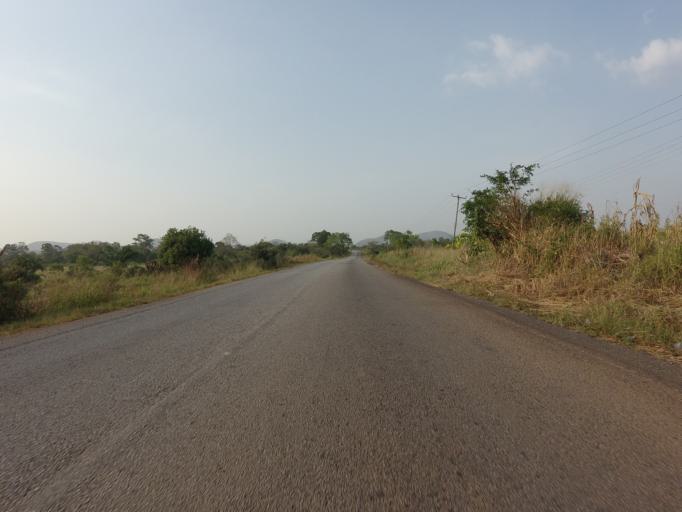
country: GH
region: Volta
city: Ho
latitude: 6.3855
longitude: 0.1851
